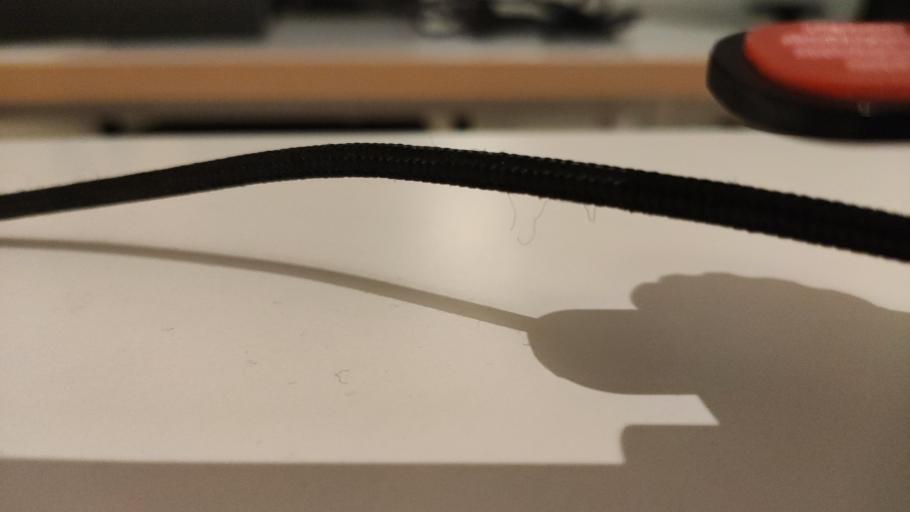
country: RU
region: Moskovskaya
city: Malino
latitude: 55.1009
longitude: 38.0729
